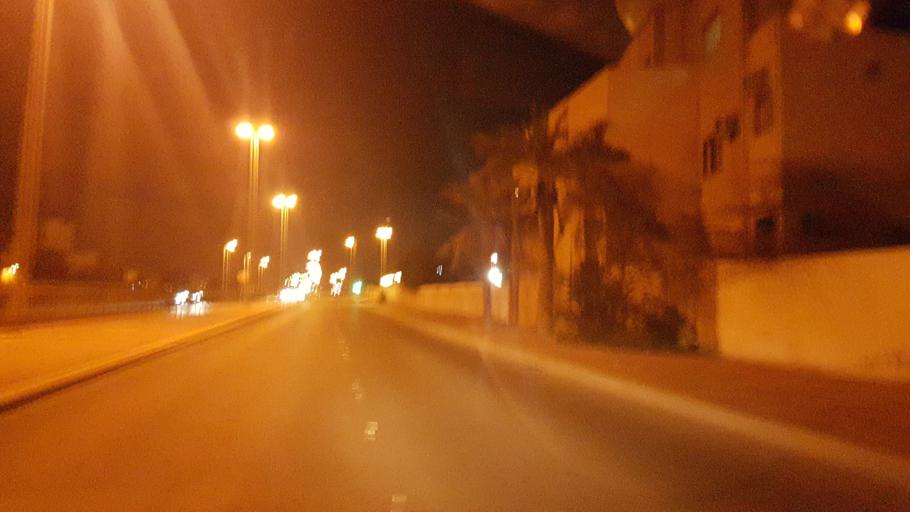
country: BH
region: Muharraq
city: Al Hadd
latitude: 26.2486
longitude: 50.6520
